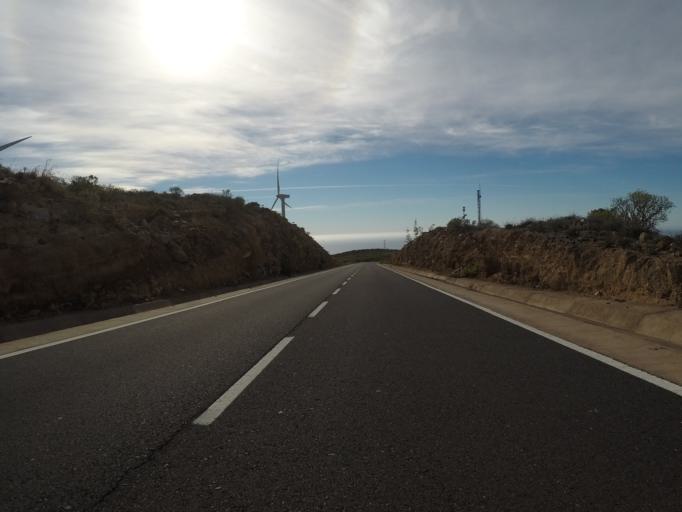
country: ES
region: Canary Islands
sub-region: Provincia de Santa Cruz de Tenerife
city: Lomo de Arico
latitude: 28.1579
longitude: -16.4838
